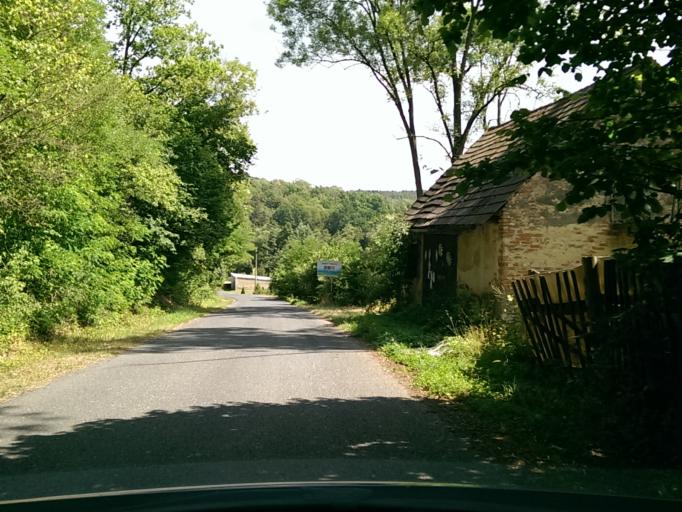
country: CZ
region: Ustecky
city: Host'ka
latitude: 50.5156
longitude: 14.3809
